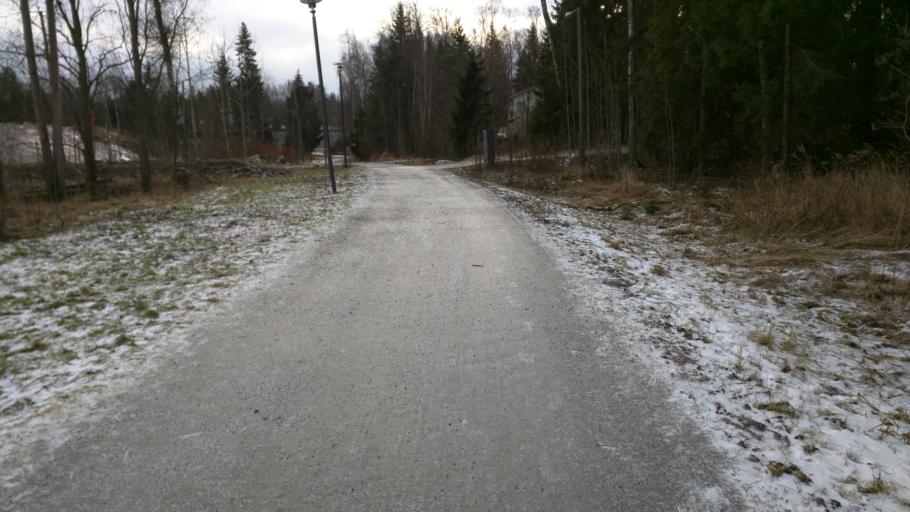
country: FI
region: Uusimaa
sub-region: Helsinki
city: Kilo
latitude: 60.1926
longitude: 24.7831
